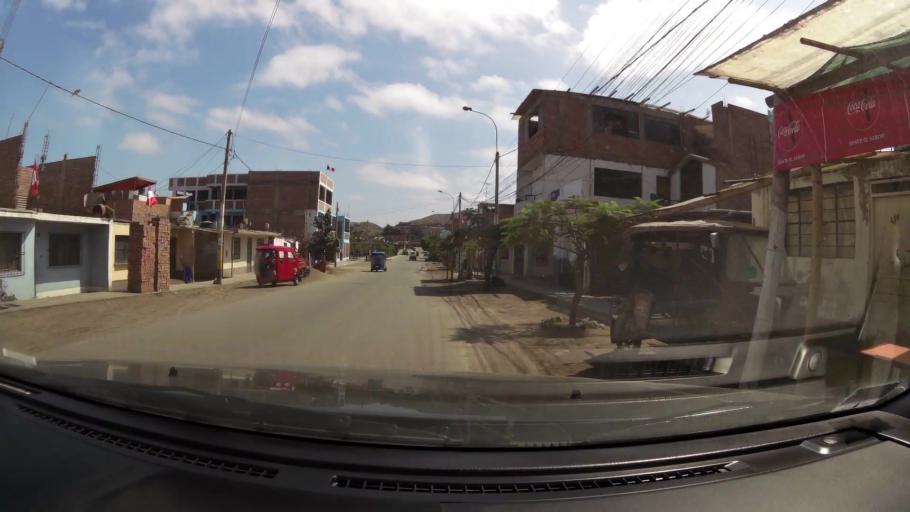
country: PE
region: Lima
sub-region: Provincia de Canete
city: Mala
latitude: -12.6550
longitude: -76.6294
